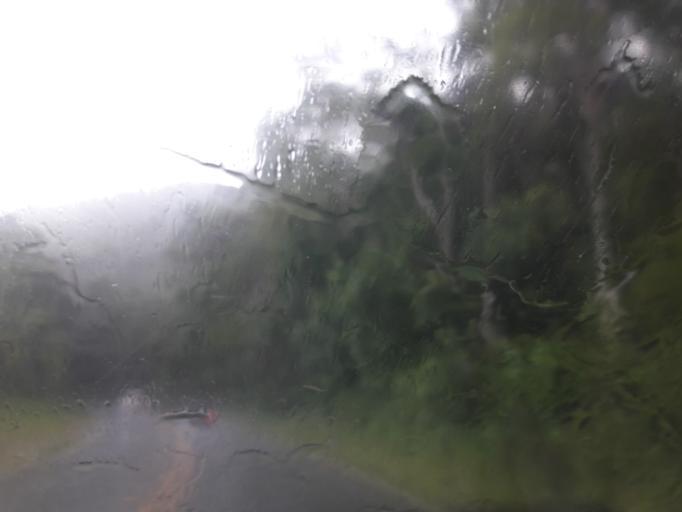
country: BR
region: Sao Paulo
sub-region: Bom Jesus Dos Perdoes
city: Bom Jesus dos Perdoes
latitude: -23.2438
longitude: -46.4114
